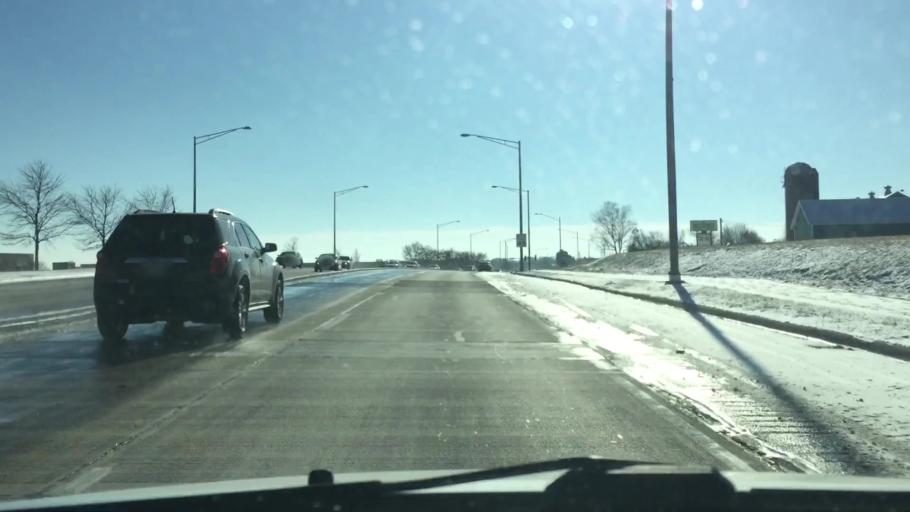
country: US
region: Illinois
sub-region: Kane County
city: Saint Charles
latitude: 41.9072
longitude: -88.2772
